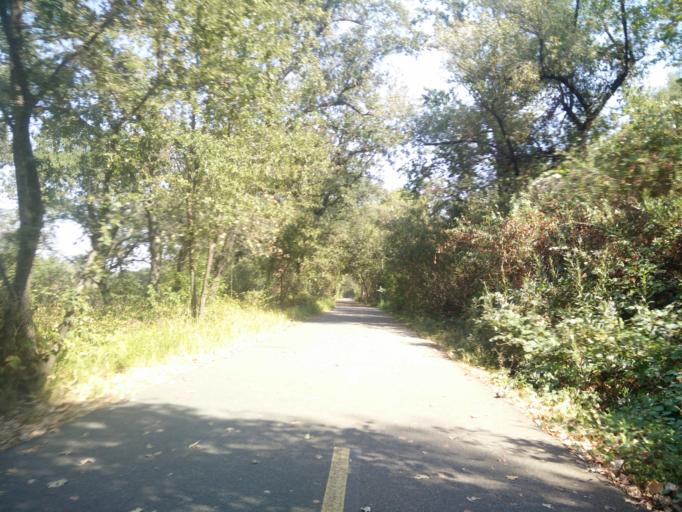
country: US
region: California
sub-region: Shasta County
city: Redding
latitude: 40.5927
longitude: -122.4210
